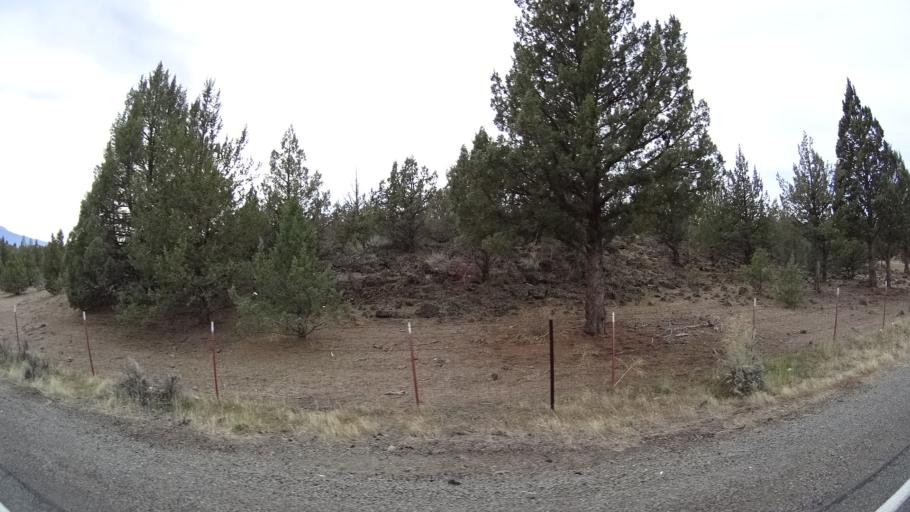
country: US
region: California
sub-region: Siskiyou County
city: Weed
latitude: 41.6072
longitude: -122.3625
